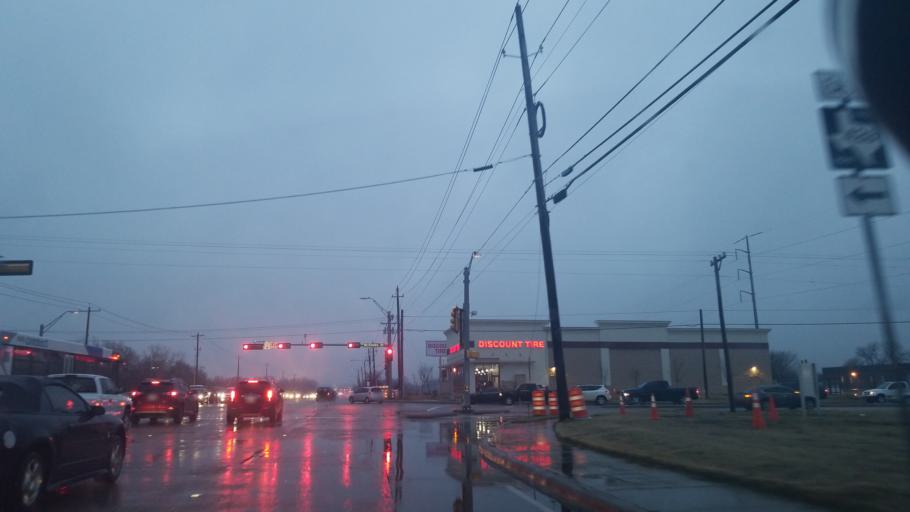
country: US
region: Texas
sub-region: Denton County
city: Denton
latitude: 33.2135
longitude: -97.0908
